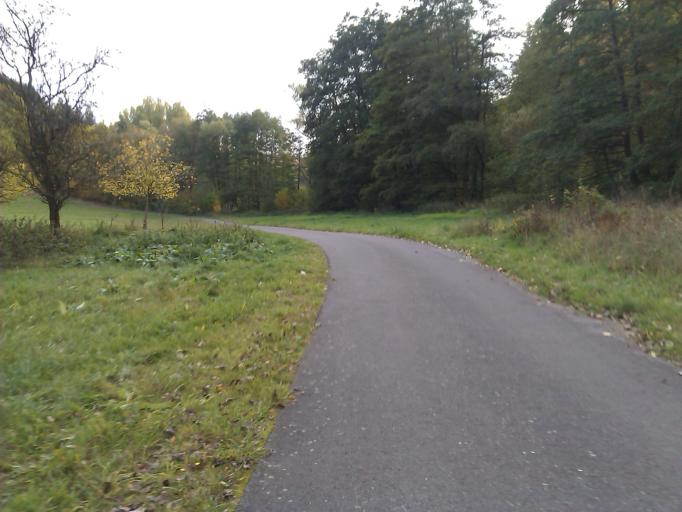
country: DE
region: Rheinland-Pfalz
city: Ginsweiler
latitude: 49.6425
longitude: 7.6537
